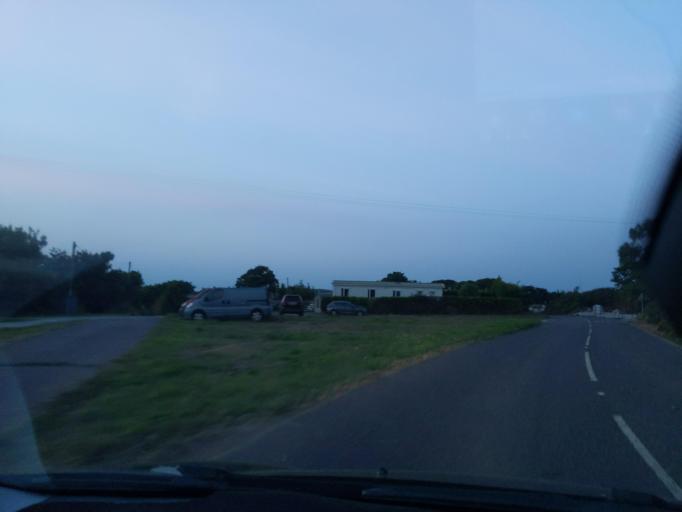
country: GB
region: England
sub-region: Cornwall
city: Camborne
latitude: 50.1858
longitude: -5.3130
